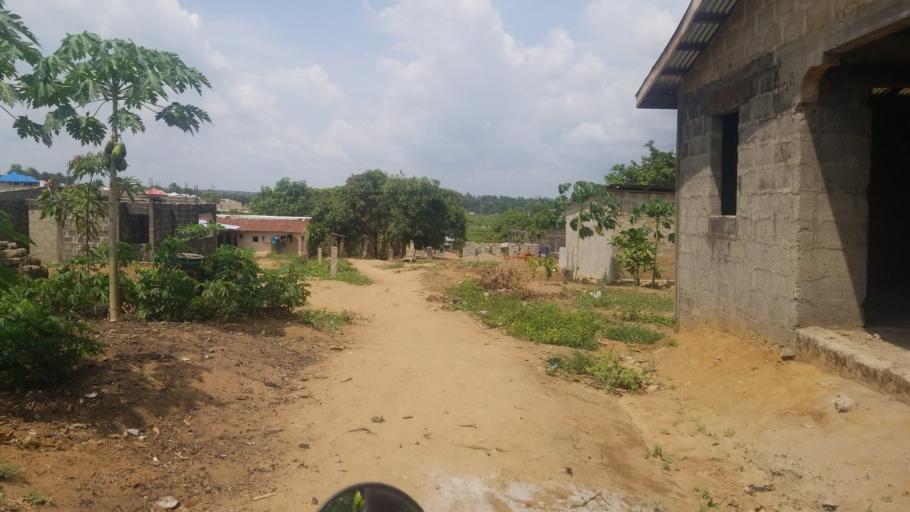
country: SL
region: Western Area
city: Waterloo
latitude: 8.3199
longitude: -13.0425
